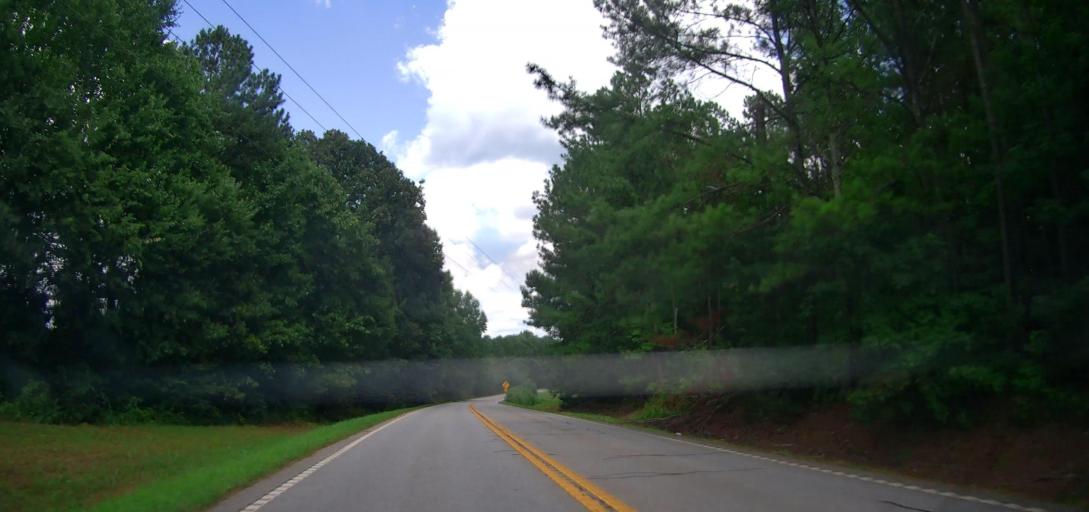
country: US
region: Georgia
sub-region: Heard County
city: Franklin
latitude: 33.3442
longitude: -85.1741
